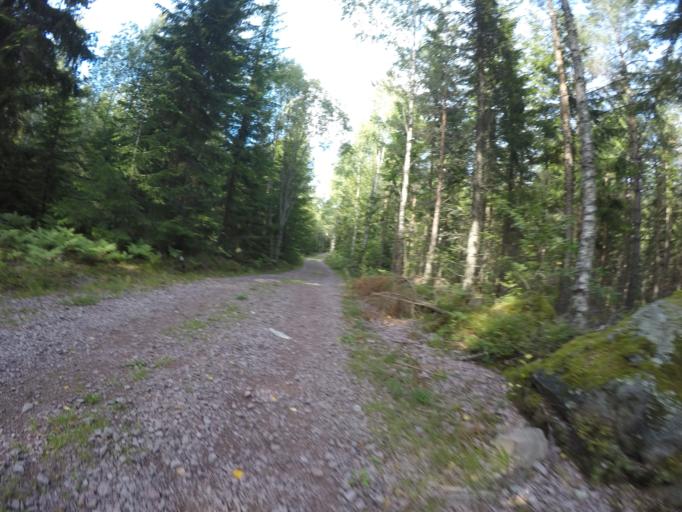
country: SE
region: Soedermanland
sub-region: Eskilstuna Kommun
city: Kvicksund
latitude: 59.5306
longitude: 16.3334
